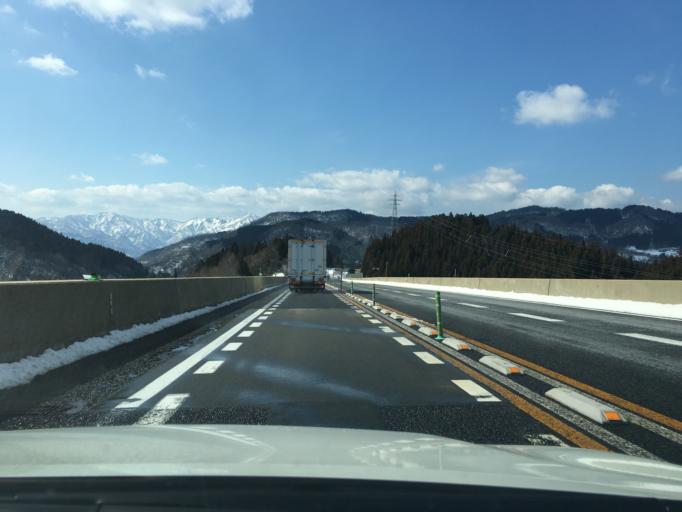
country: JP
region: Yamagata
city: Tsuruoka
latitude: 38.5882
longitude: 139.8953
